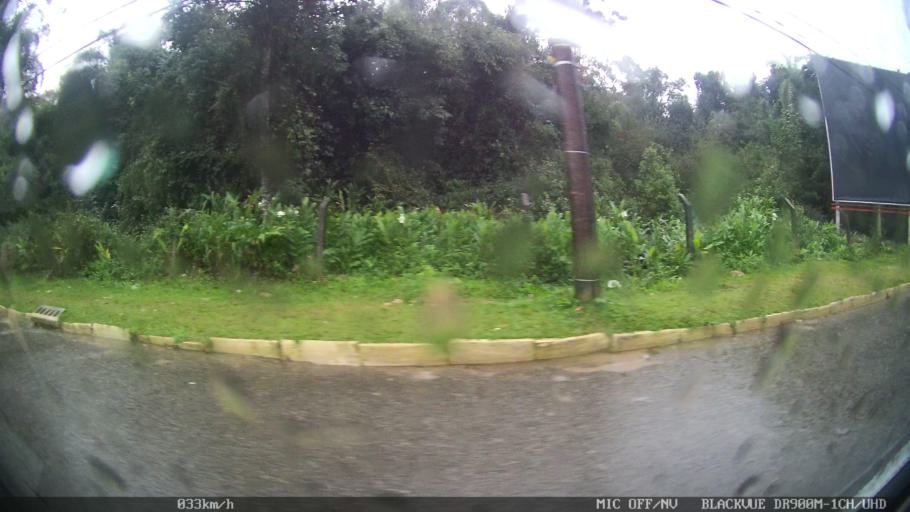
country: BR
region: Santa Catarina
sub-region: Itajai
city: Itajai
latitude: -26.9439
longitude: -48.6392
